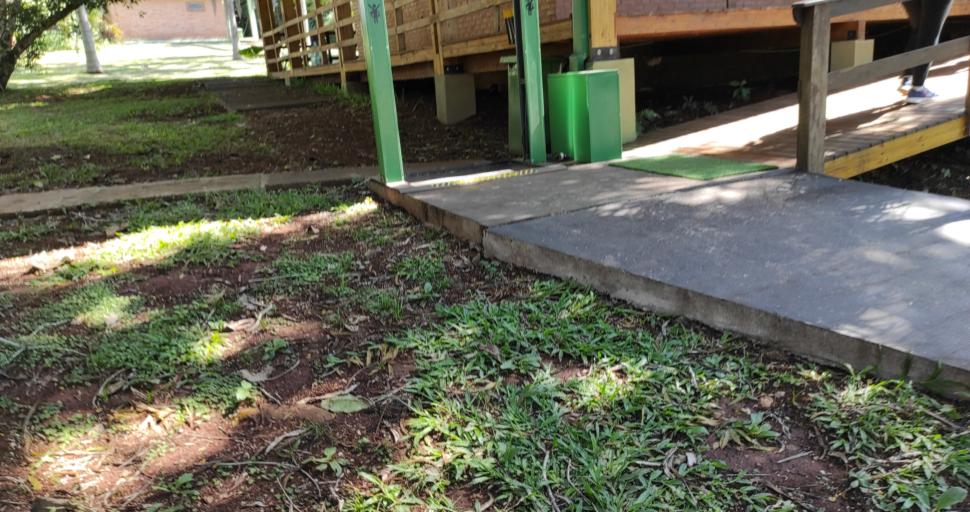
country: BR
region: Rio Grande do Sul
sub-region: Tres Passos
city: Tres Passos
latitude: -27.1531
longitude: -53.9015
